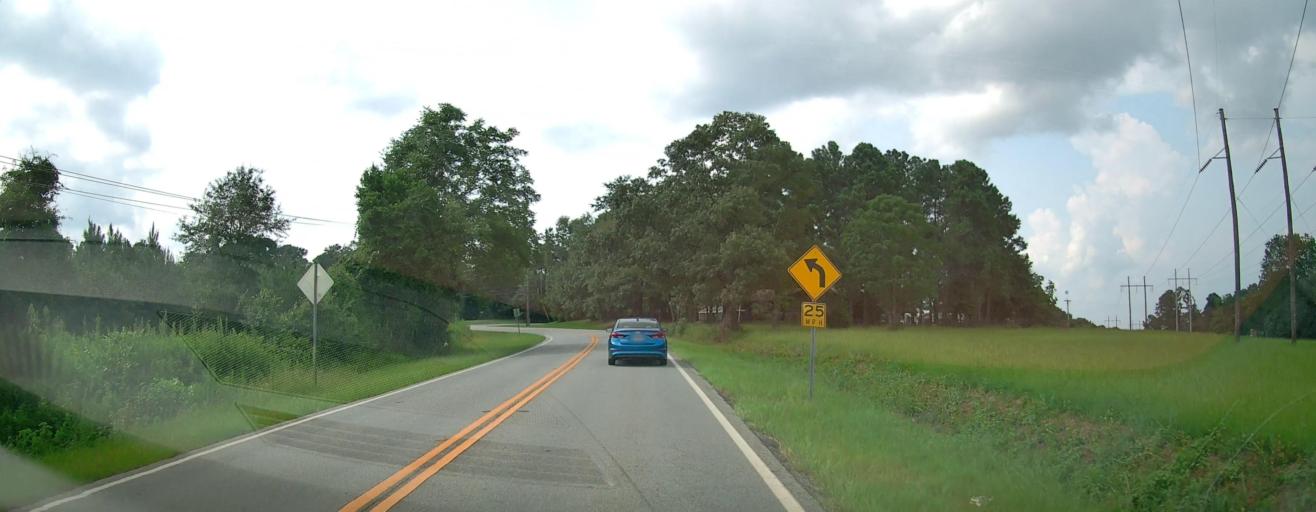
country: US
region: Georgia
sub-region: Houston County
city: Robins Air Force Base
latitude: 32.5754
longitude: -83.6102
